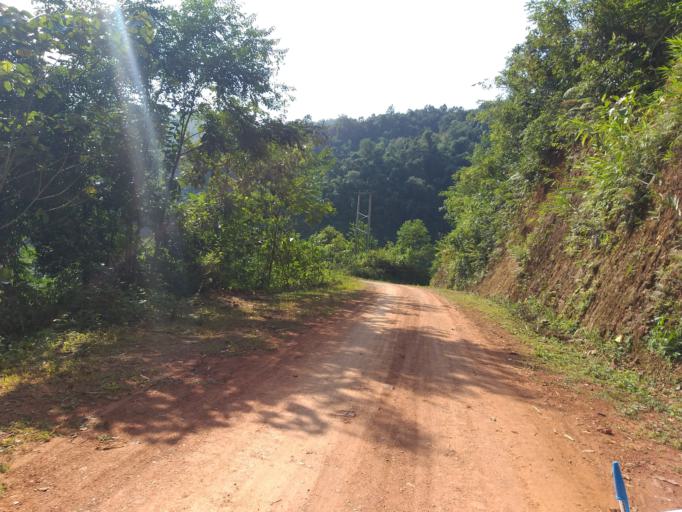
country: LA
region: Phongsali
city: Khoa
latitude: 21.1967
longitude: 102.6645
